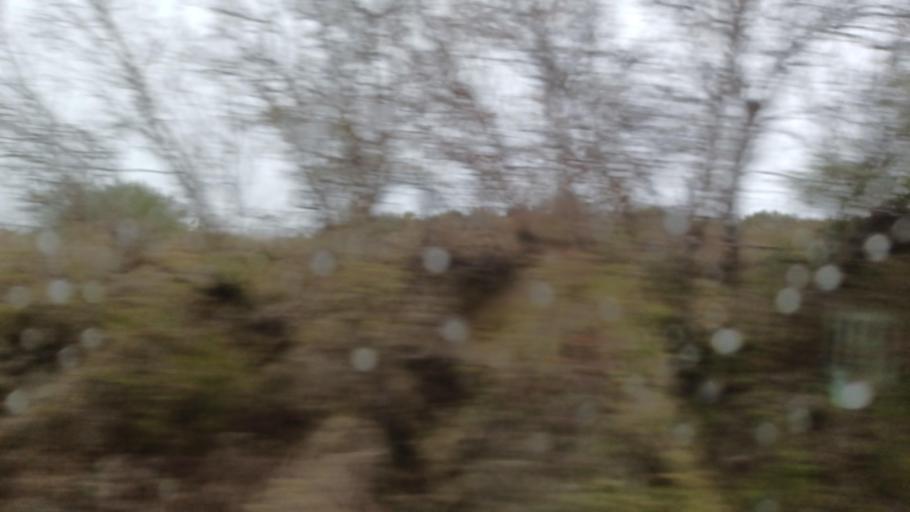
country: CY
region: Limassol
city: Pachna
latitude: 34.7798
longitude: 32.8207
